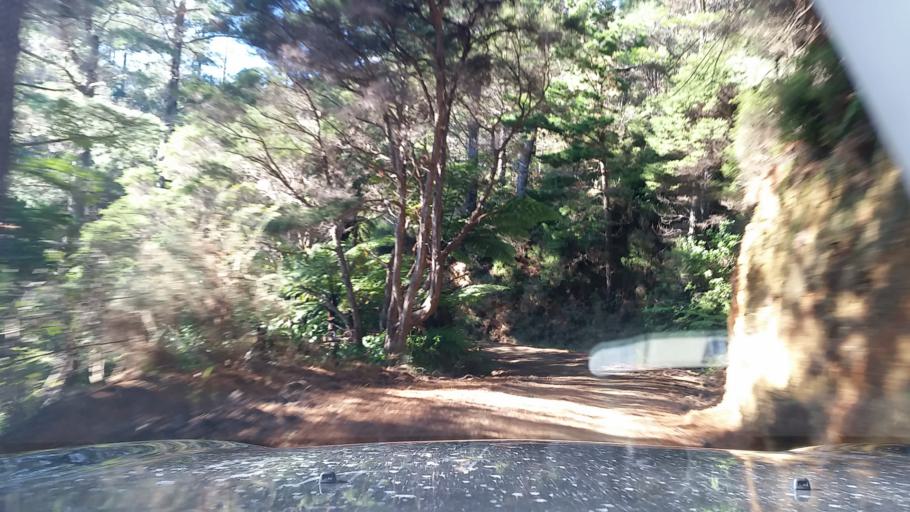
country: NZ
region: Marlborough
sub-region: Marlborough District
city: Picton
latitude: -41.1205
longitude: 173.9894
